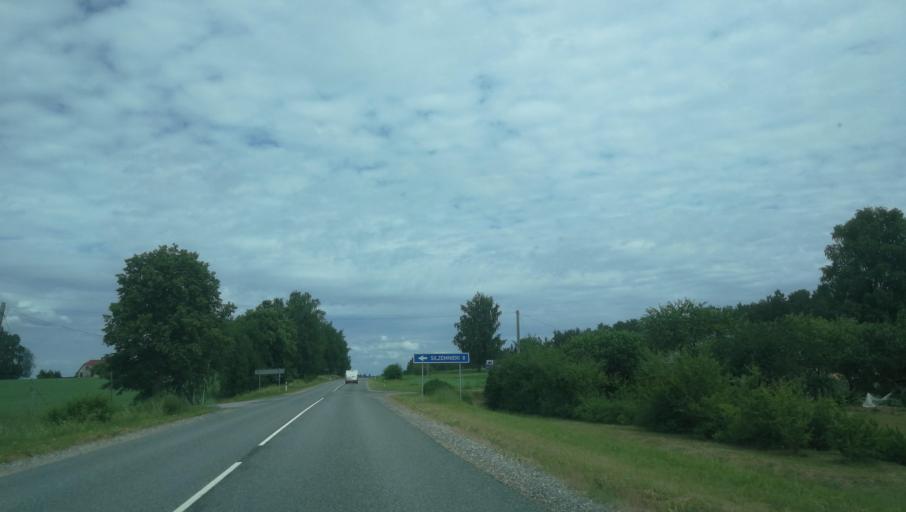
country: LV
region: Naukseni
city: Naukseni
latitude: 57.7328
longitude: 25.4242
